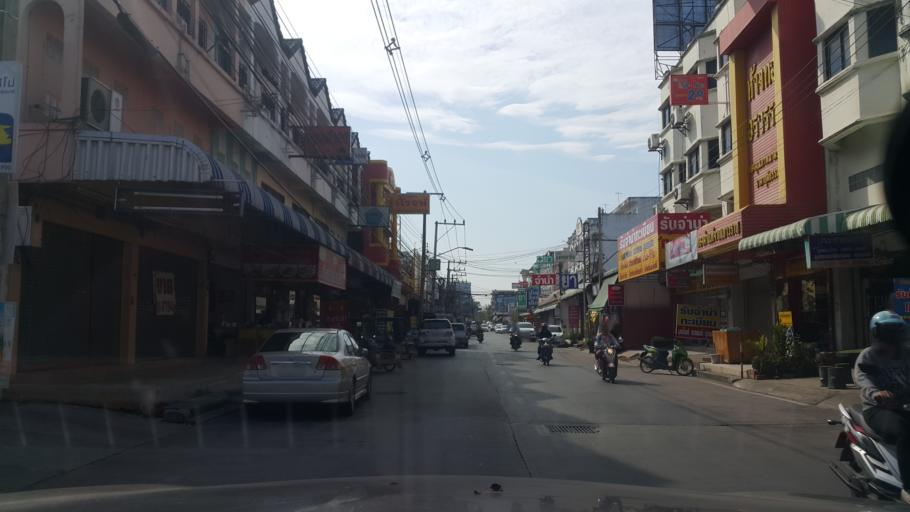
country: TH
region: Nakhon Ratchasima
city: Nakhon Ratchasima
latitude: 14.9511
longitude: 102.0445
